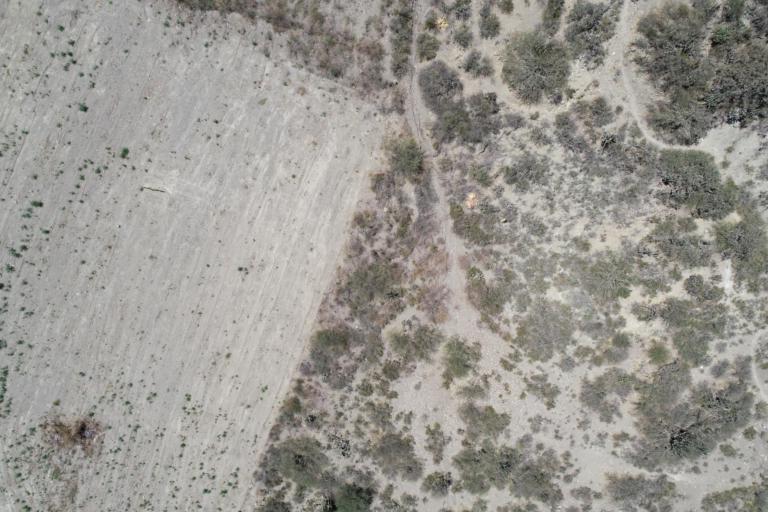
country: BO
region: La Paz
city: La Paz
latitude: -16.6429
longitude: -68.0397
